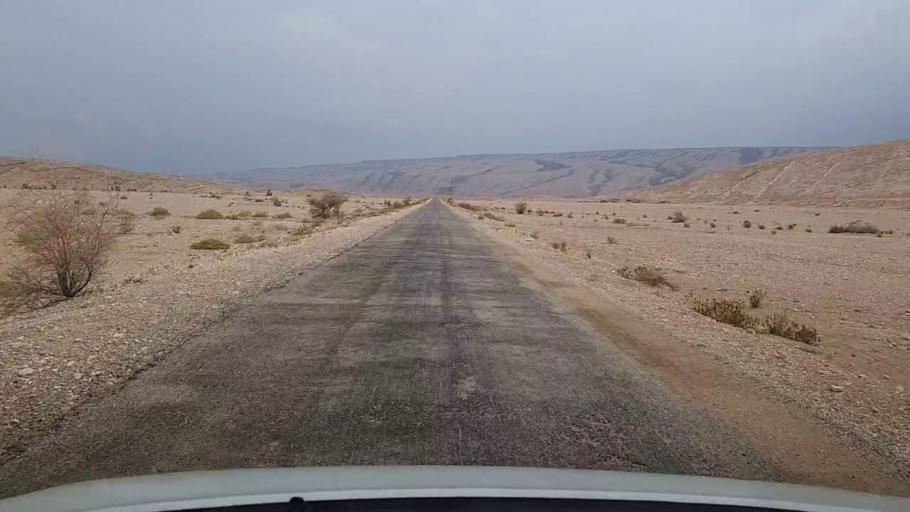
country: PK
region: Sindh
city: Sehwan
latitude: 26.2340
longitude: 67.7096
